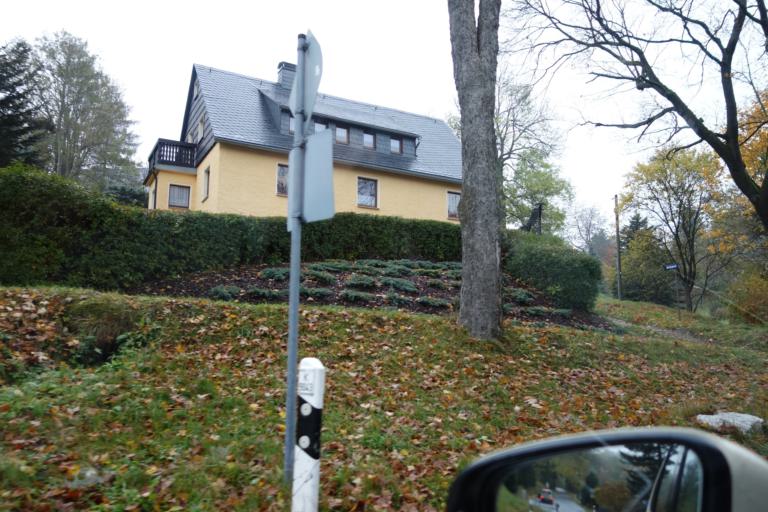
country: DE
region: Saxony
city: Schmiedeberg
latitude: 50.7571
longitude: 13.6328
